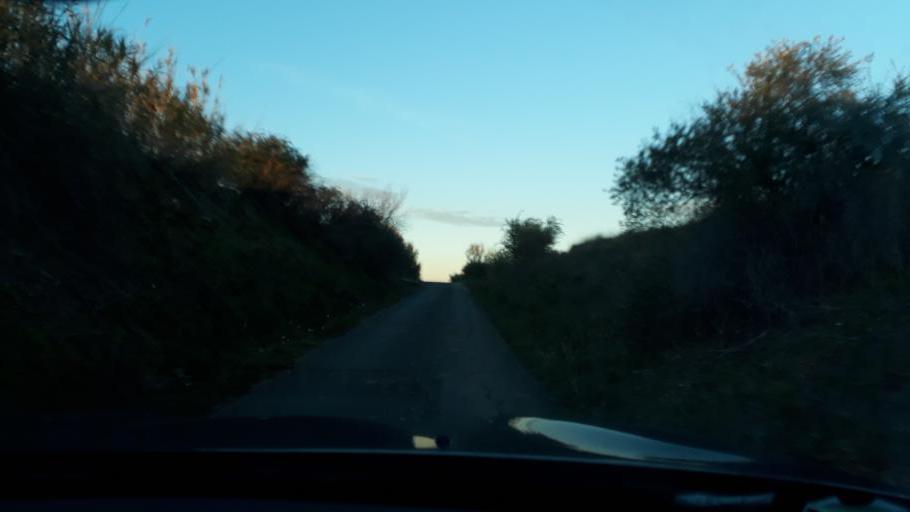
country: FR
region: Languedoc-Roussillon
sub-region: Departement de l'Herault
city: Florensac
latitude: 43.3981
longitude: 3.4593
